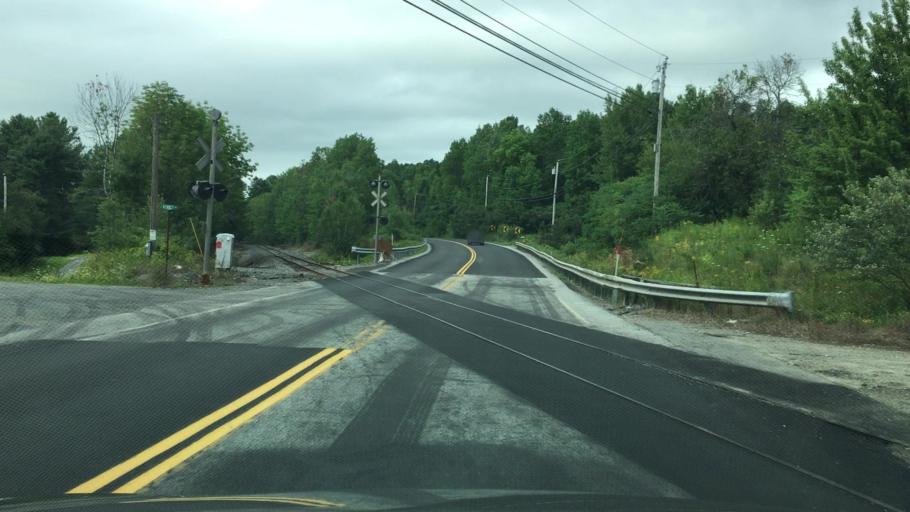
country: US
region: Maine
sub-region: Waldo County
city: Winterport
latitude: 44.6164
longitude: -68.8267
